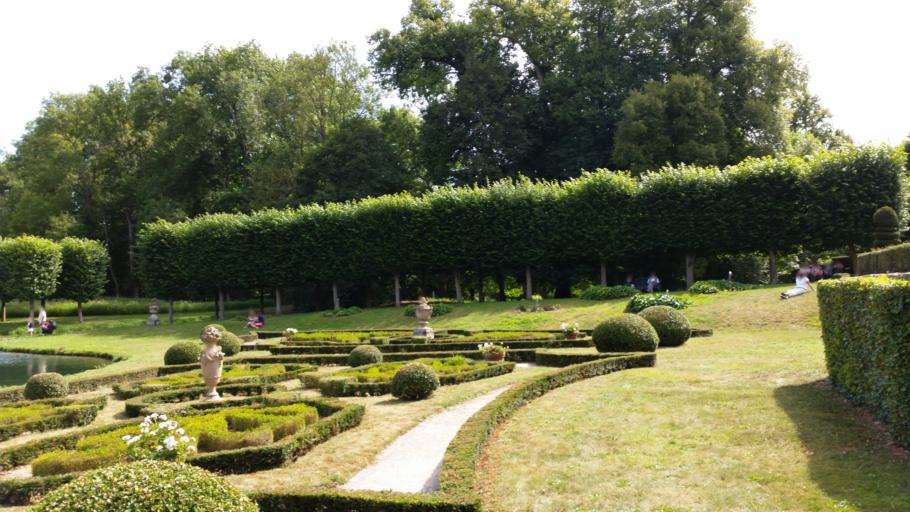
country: FR
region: Lower Normandy
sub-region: Departement du Calvados
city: Saint-Pierre-sur-Dives
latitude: 48.9871
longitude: -0.0784
